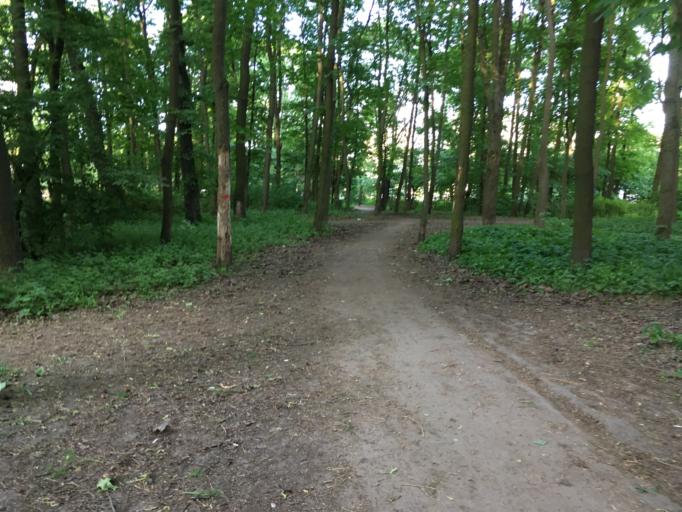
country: RU
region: St.-Petersburg
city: Kushelevka
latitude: 59.9945
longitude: 30.3522
